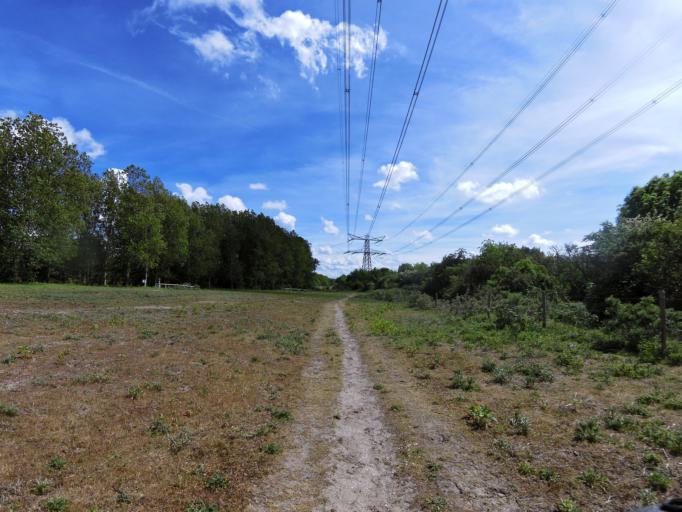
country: NL
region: South Holland
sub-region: Gemeente Rotterdam
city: Hoek van Holland
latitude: 51.9245
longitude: 4.1014
